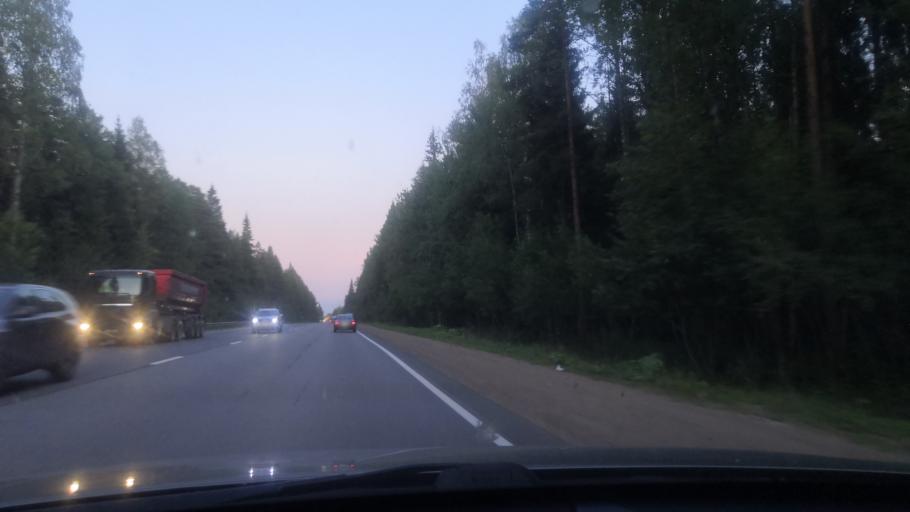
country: RU
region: St.-Petersburg
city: Pesochnyy
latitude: 60.1848
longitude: 30.1175
